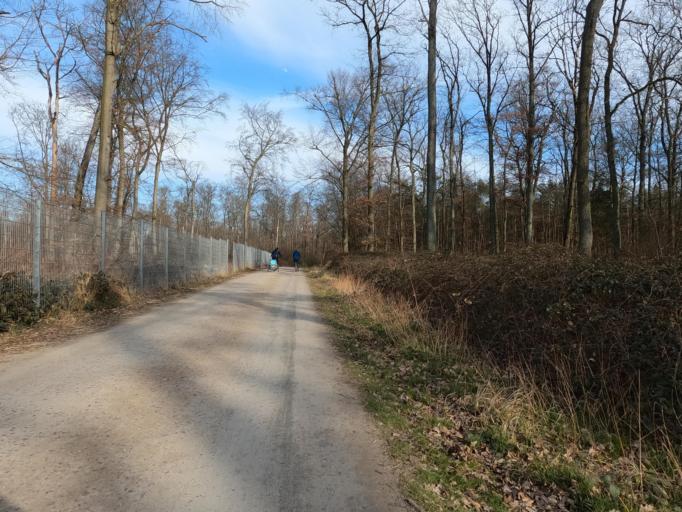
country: DE
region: Hesse
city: Raunheim
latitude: 50.0121
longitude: 8.4863
